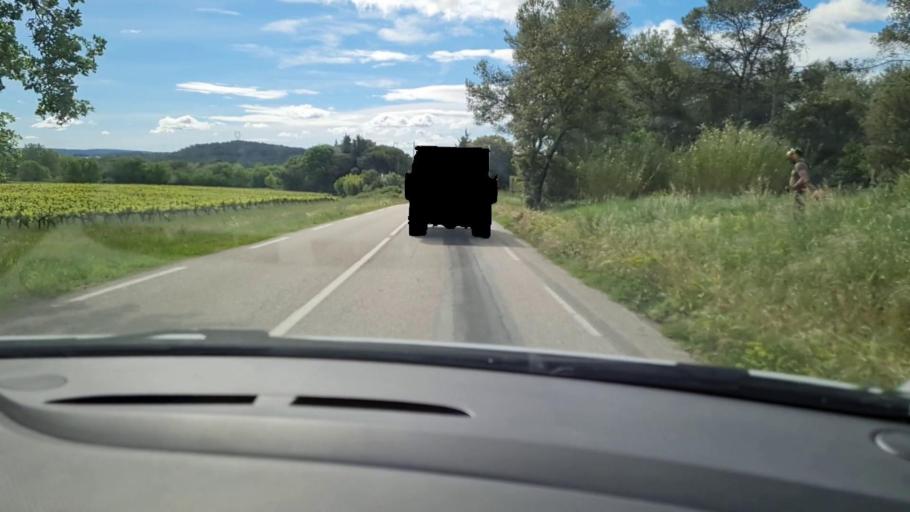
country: FR
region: Languedoc-Roussillon
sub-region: Departement du Gard
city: Sommieres
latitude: 43.8354
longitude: 4.0347
